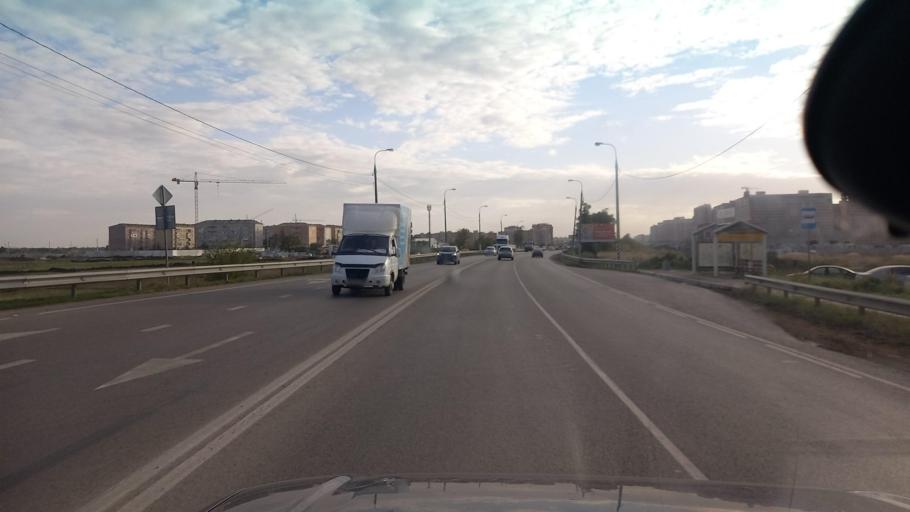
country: RU
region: Krasnodarskiy
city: Krasnodar
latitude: 45.1028
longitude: 38.9164
